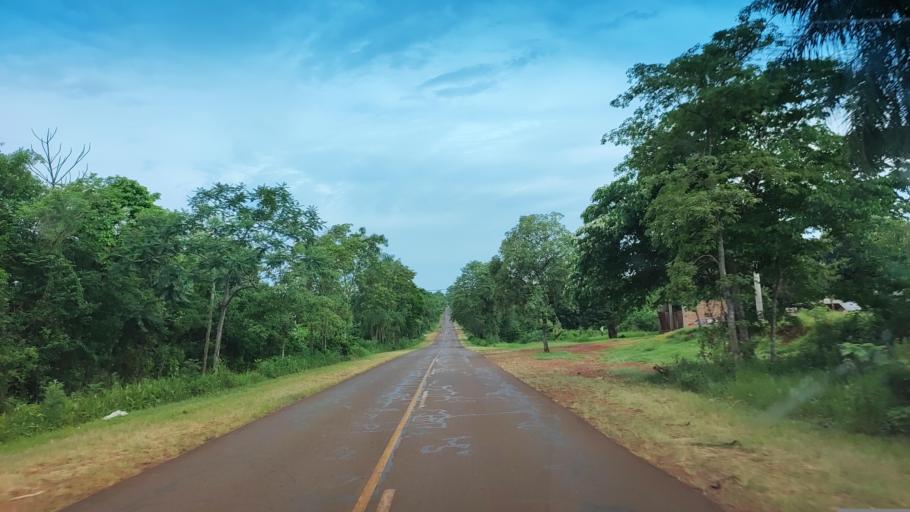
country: AR
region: Misiones
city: Gobernador Roca
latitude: -27.1377
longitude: -55.5017
